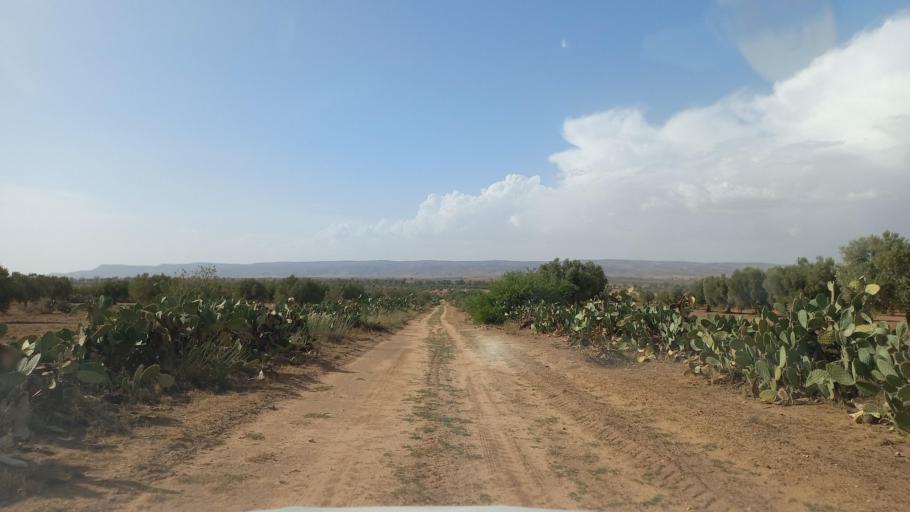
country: TN
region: Al Qasrayn
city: Kasserine
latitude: 35.2139
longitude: 8.9510
